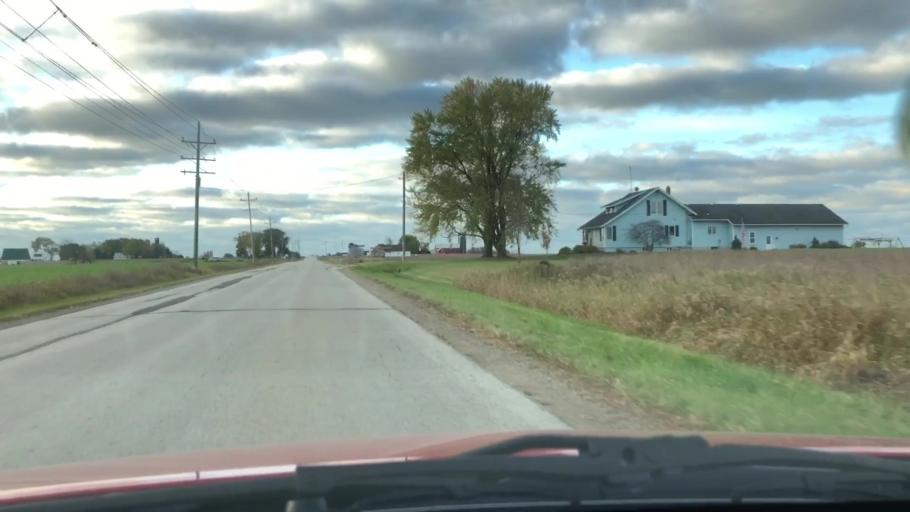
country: US
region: Wisconsin
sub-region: Outagamie County
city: Seymour
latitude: 44.5066
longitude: -88.3104
